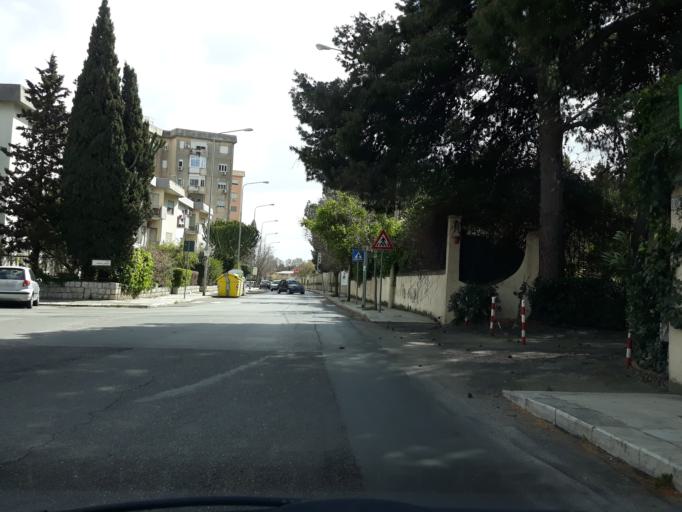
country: IT
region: Sicily
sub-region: Palermo
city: Palermo
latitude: 38.1239
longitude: 13.3182
